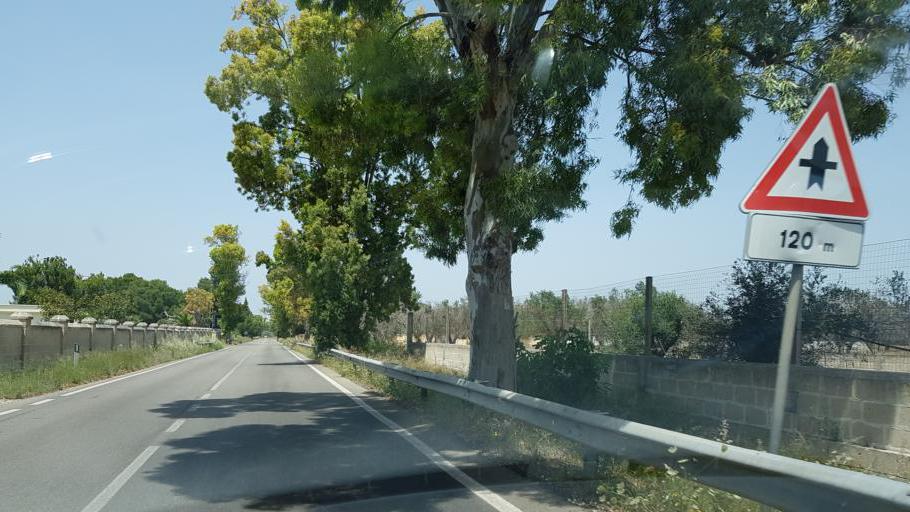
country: IT
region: Apulia
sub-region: Provincia di Lecce
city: Porto Cesareo
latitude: 40.2612
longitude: 17.9206
